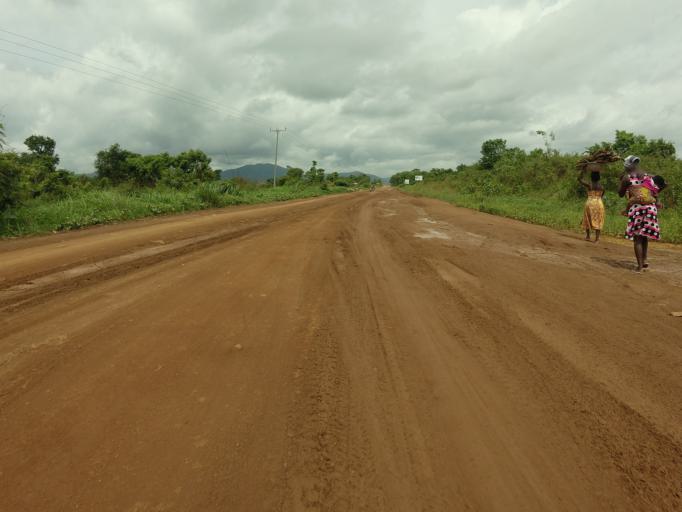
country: GH
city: Kpandae
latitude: 8.2779
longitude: 0.5086
